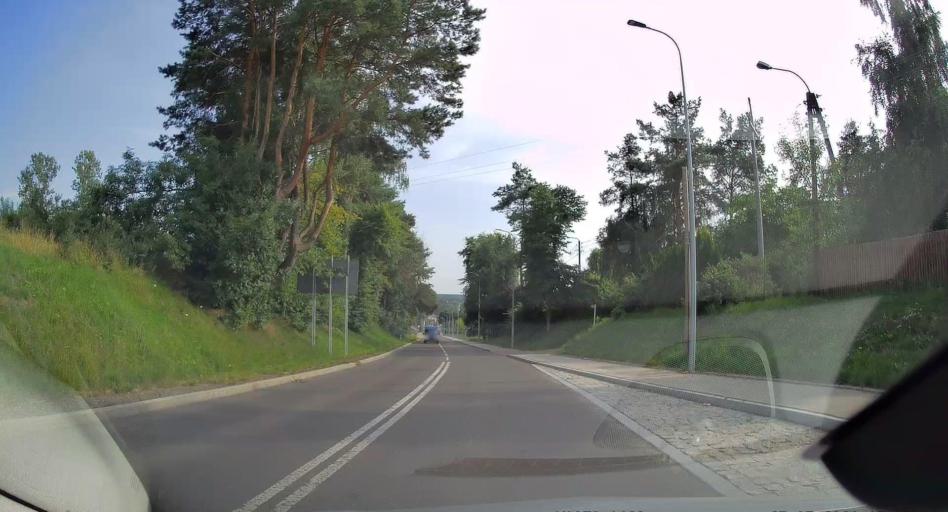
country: PL
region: Lodz Voivodeship
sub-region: Powiat tomaszowski
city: Inowlodz
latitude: 51.5303
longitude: 20.2229
